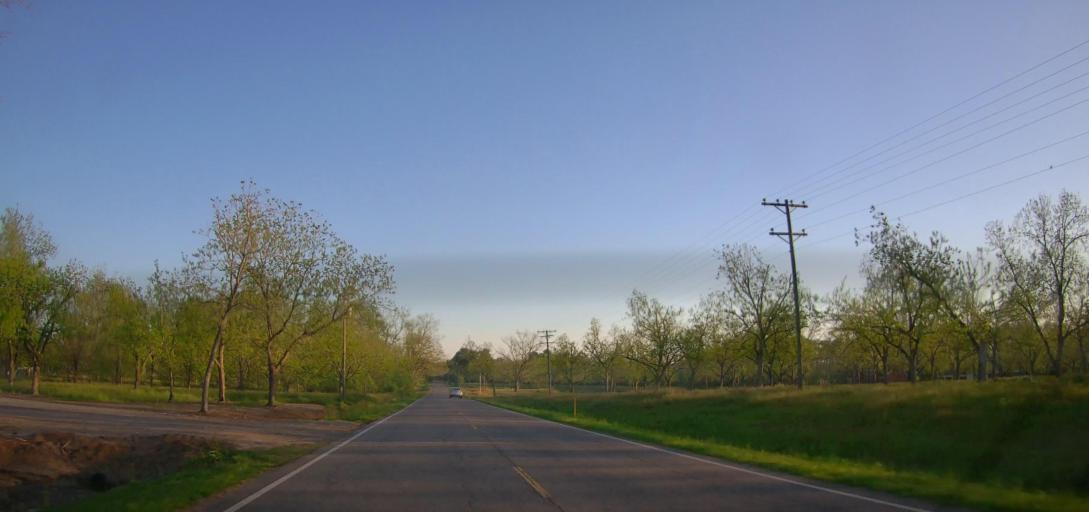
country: US
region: Georgia
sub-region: Irwin County
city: Ocilla
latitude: 31.6029
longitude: -83.2590
